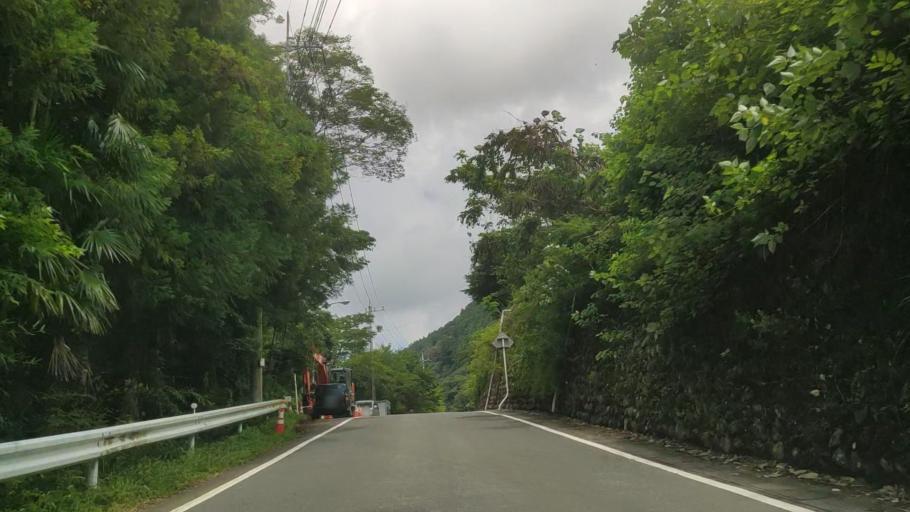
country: JP
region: Shizuoka
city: Fujinomiya
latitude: 35.2438
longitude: 138.4940
